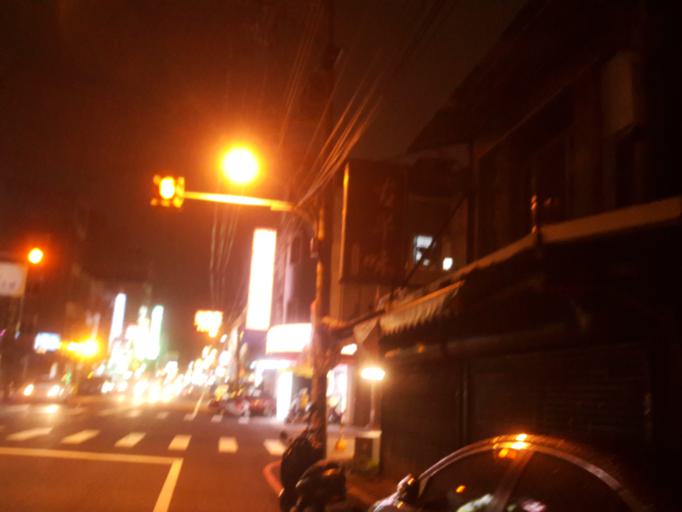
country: TW
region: Taiwan
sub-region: Hsinchu
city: Zhubei
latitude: 24.8421
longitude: 120.9985
